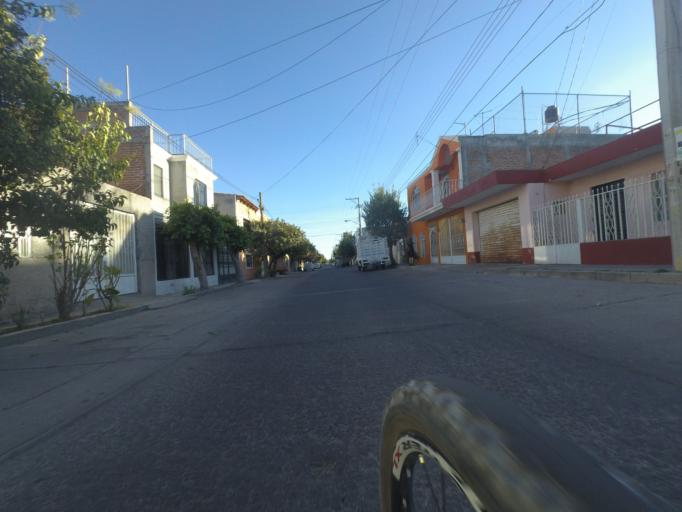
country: MX
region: Aguascalientes
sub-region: Aguascalientes
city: La Loma de los Negritos
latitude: 21.8561
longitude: -102.3416
